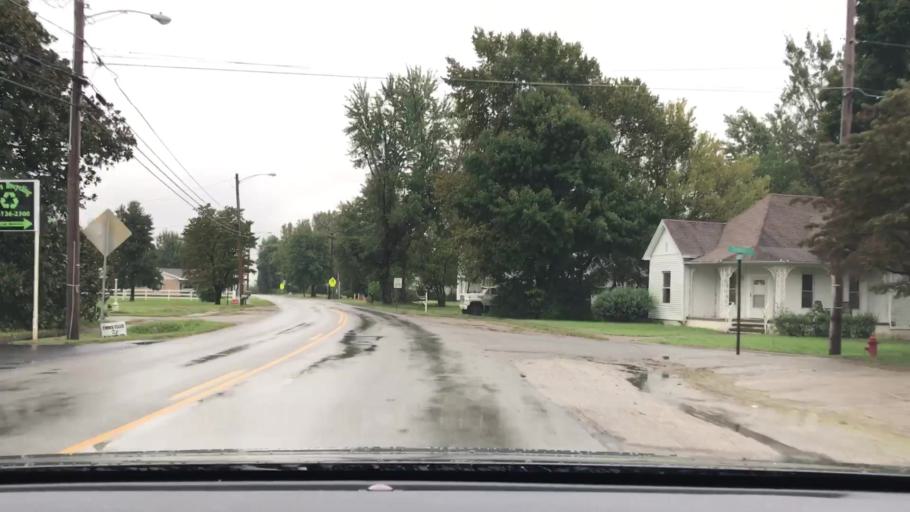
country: US
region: Kentucky
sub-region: McLean County
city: Calhoun
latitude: 37.4149
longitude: -87.2658
